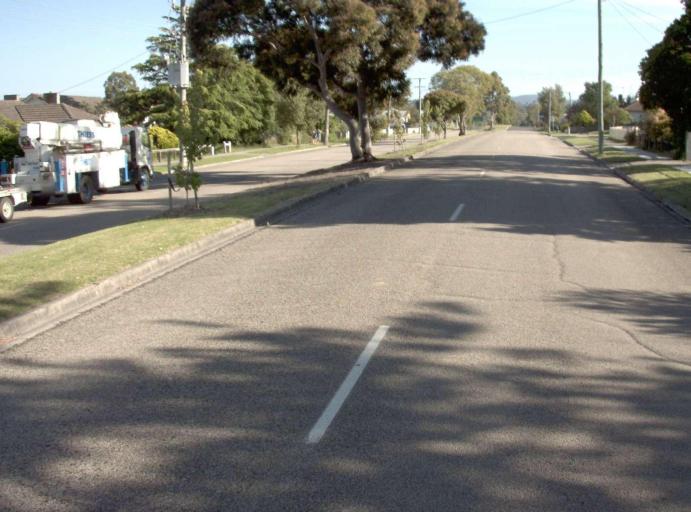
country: AU
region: Victoria
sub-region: East Gippsland
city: Lakes Entrance
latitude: -37.6992
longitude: 148.4569
